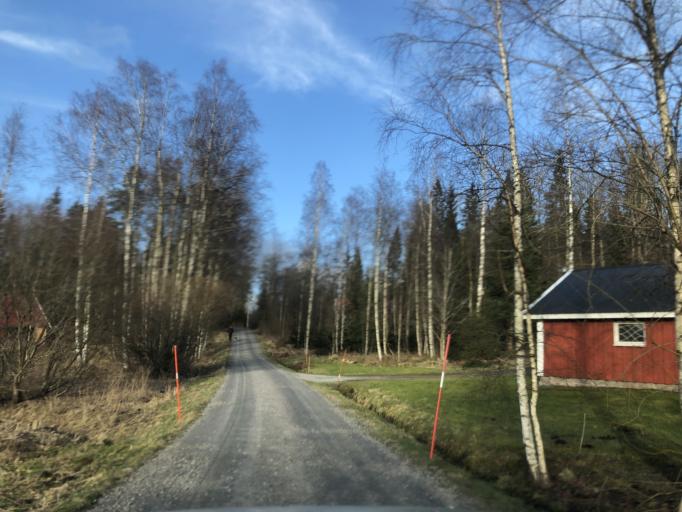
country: SE
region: Vaestra Goetaland
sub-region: Ulricehamns Kommun
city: Ulricehamn
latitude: 57.7583
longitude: 13.4532
